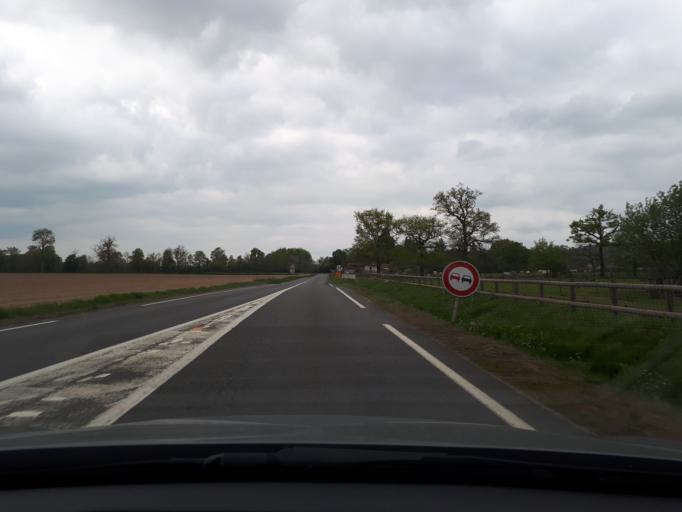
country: FR
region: Rhone-Alpes
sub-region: Departement de la Loire
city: Bellegarde-en-Forez
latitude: 45.7095
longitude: 4.2992
